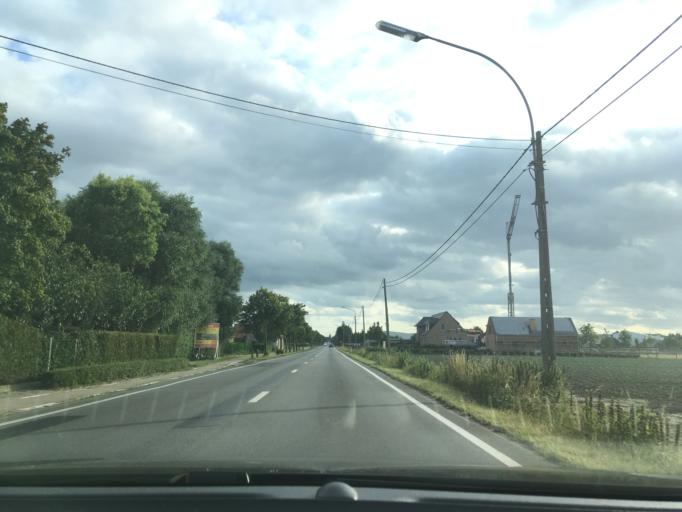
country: BE
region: Flanders
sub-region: Provincie West-Vlaanderen
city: Staden
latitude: 50.9507
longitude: 3.0409
